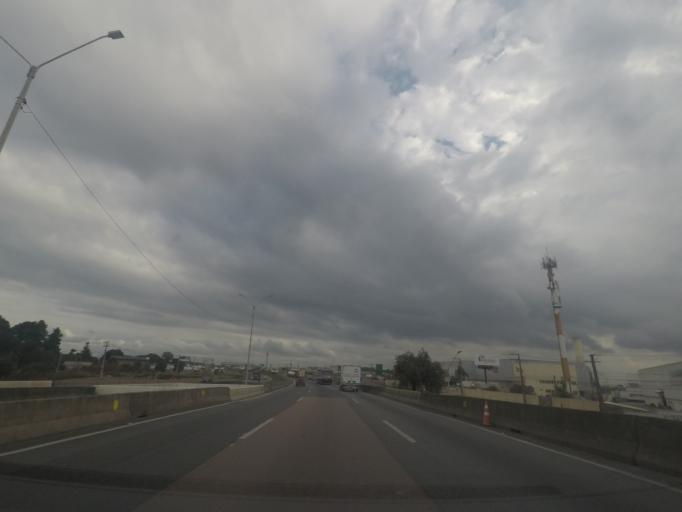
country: BR
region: Parana
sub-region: Sao Jose Dos Pinhais
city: Sao Jose dos Pinhais
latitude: -25.5366
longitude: -49.1491
